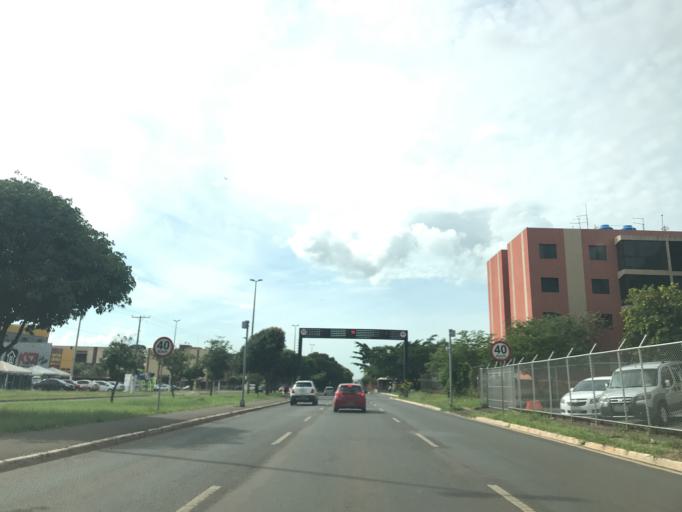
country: BR
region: Federal District
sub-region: Brasilia
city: Brasilia
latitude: -15.8124
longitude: -48.0895
